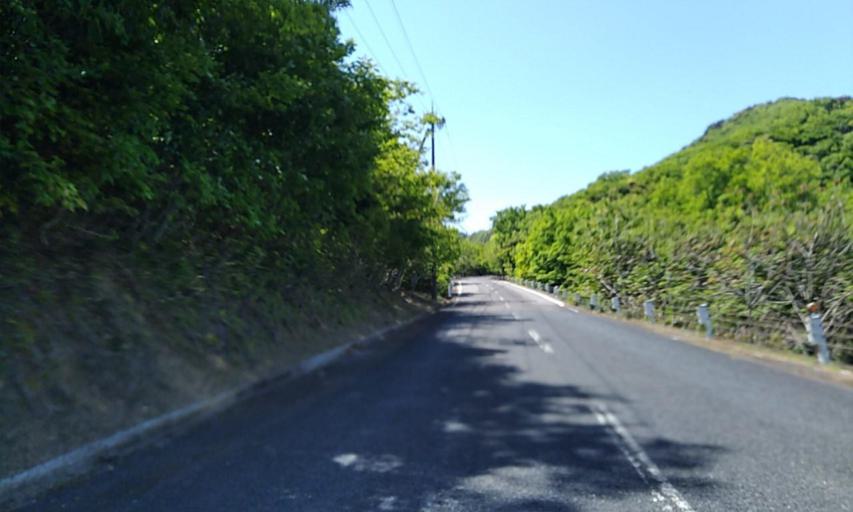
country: JP
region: Fukui
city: Obama
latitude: 35.5436
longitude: 135.7490
